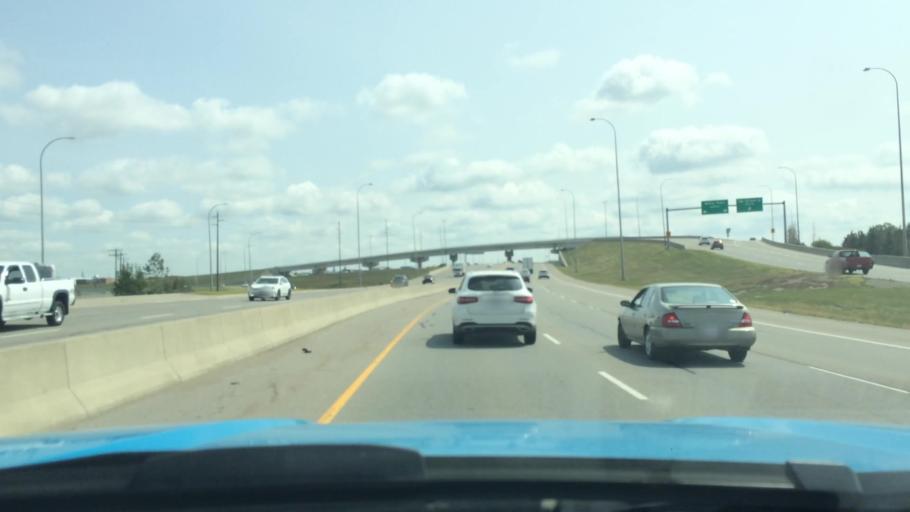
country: CA
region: Alberta
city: Calgary
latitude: 51.0956
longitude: -113.9886
